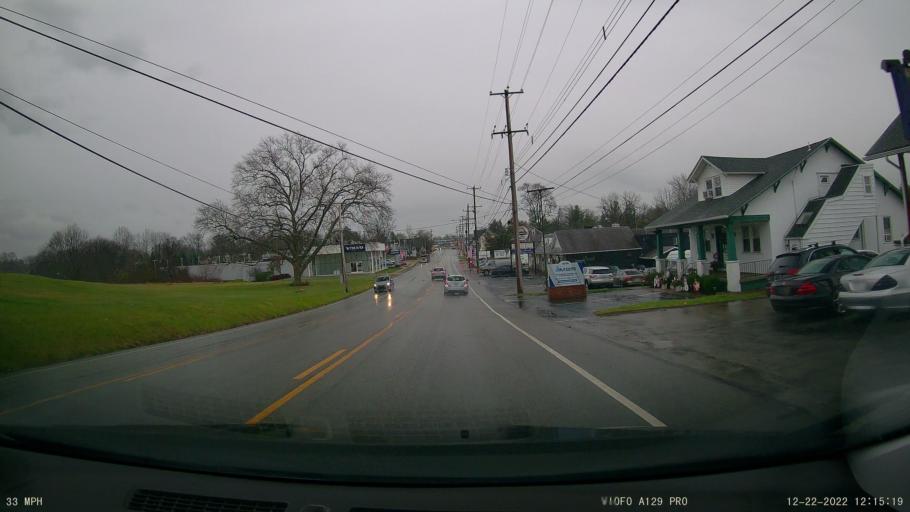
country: US
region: Pennsylvania
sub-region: Montgomery County
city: West Norriton
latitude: 40.1350
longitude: -75.3811
